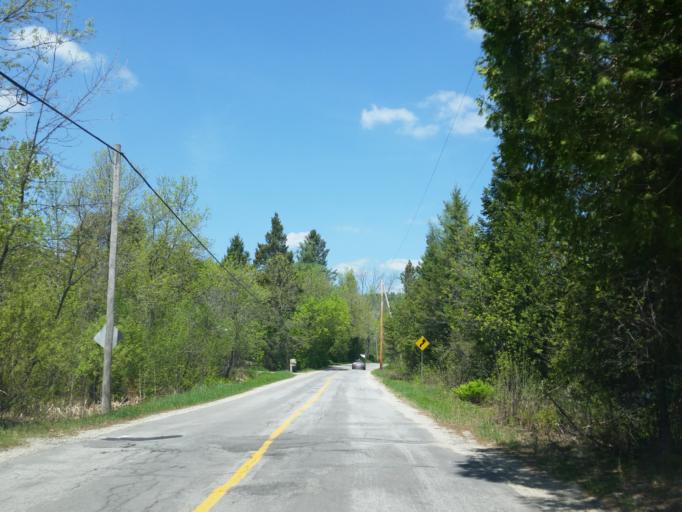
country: CA
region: Quebec
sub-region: Outaouais
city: Wakefield
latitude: 45.6266
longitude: -75.9067
